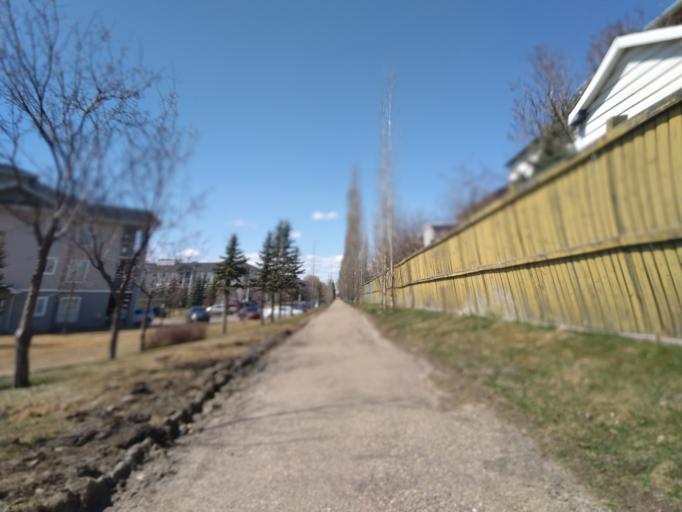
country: CA
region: Alberta
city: Chestermere
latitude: 51.0397
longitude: -113.9251
